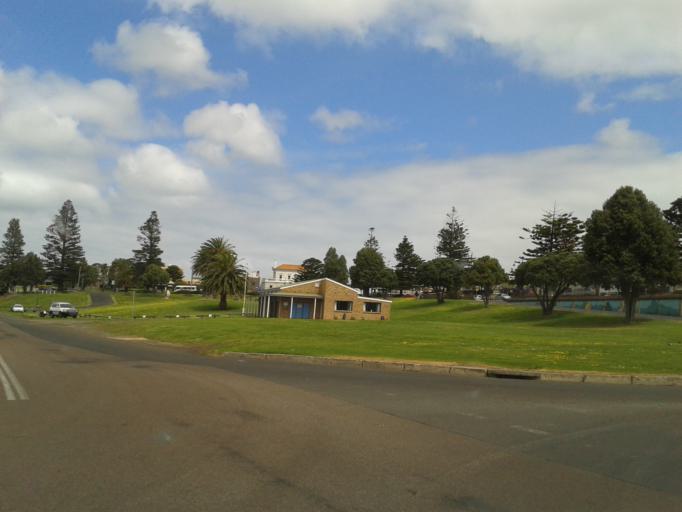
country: AU
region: Victoria
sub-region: Glenelg
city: Portland
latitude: -38.3485
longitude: 141.6072
